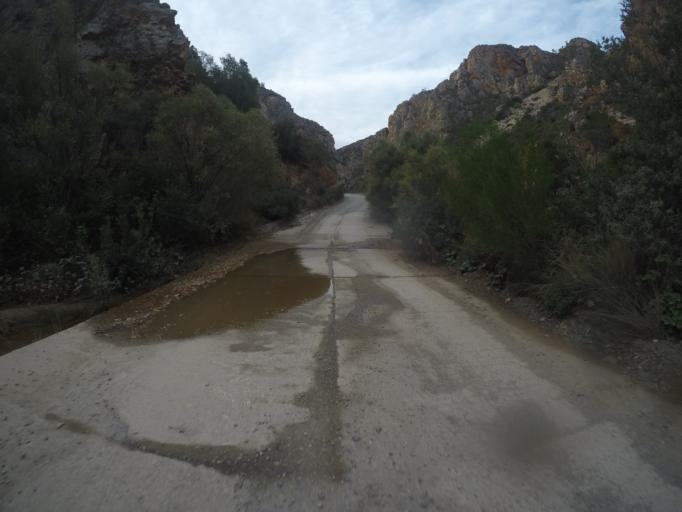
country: ZA
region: Eastern Cape
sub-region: Cacadu District Municipality
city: Willowmore
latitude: -33.5114
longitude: 23.6400
